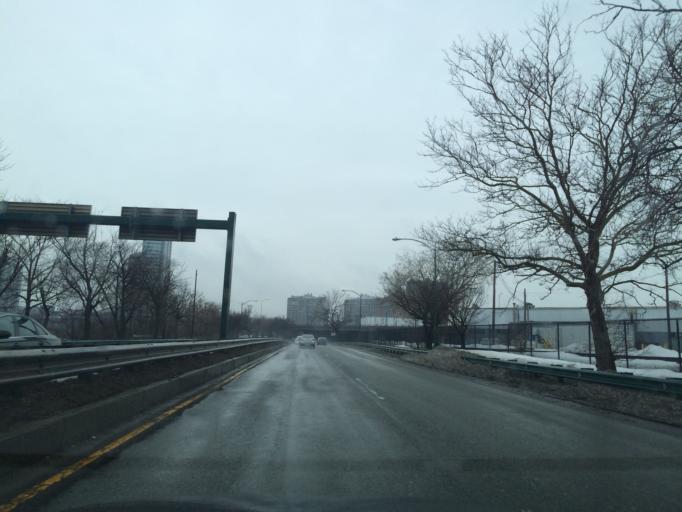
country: US
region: Massachusetts
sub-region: Middlesex County
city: Cambridge
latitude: 42.3585
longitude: -71.1179
